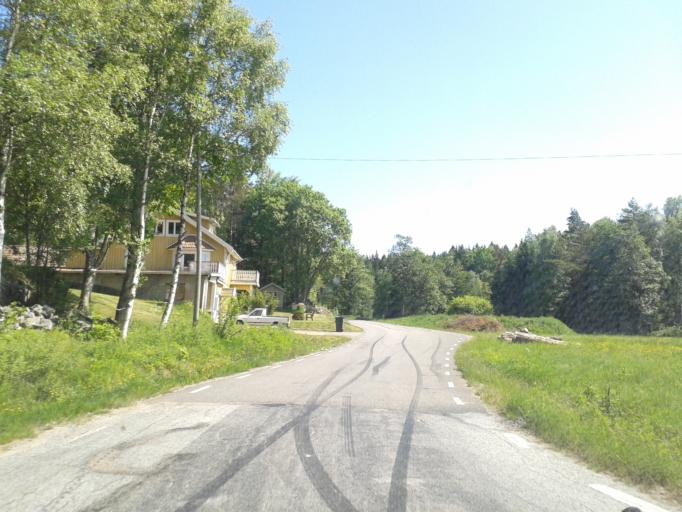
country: SE
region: Vaestra Goetaland
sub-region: Kungalvs Kommun
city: Diserod
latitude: 57.9745
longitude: 11.9720
